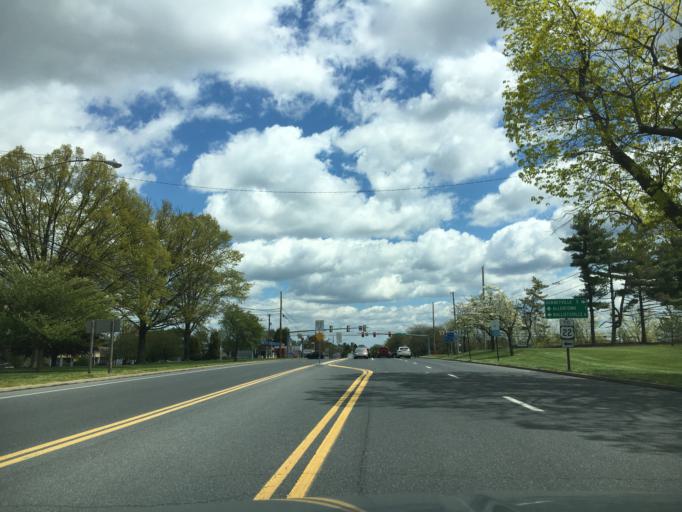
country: US
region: Pennsylvania
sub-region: Lehigh County
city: Dorneyville
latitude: 40.5972
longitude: -75.5294
